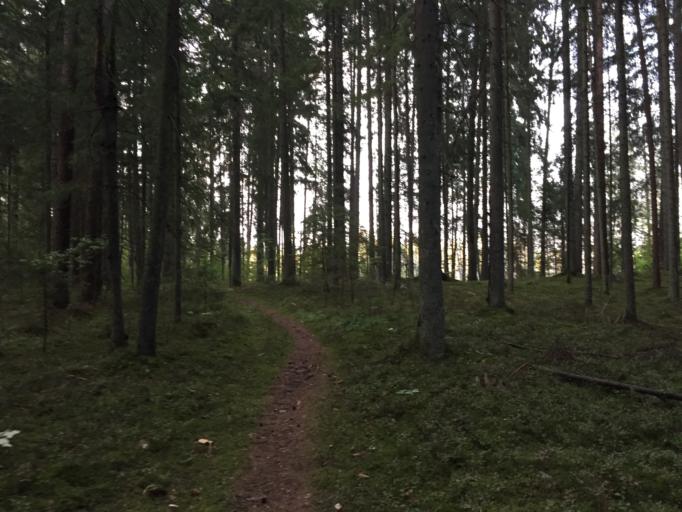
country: LV
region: Baldone
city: Baldone
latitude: 56.7565
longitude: 24.4039
